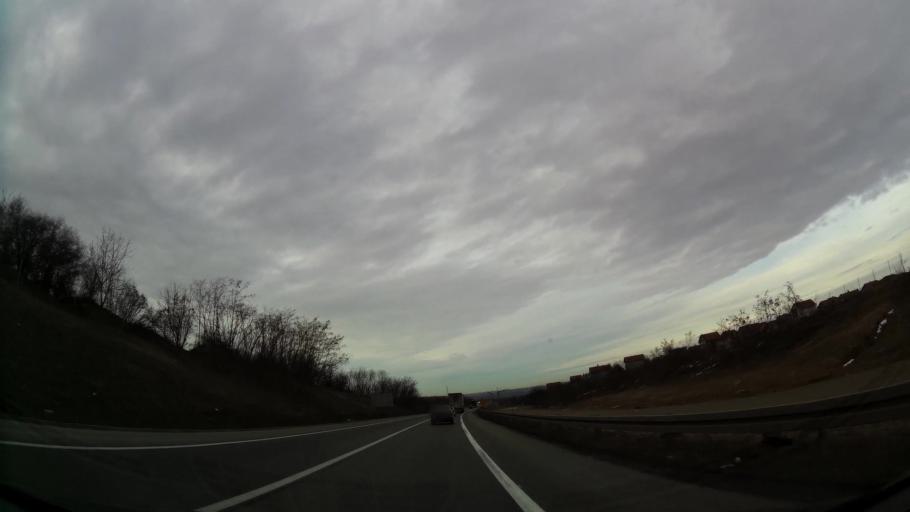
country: RS
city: Ostruznica
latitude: 44.7154
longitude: 20.3619
